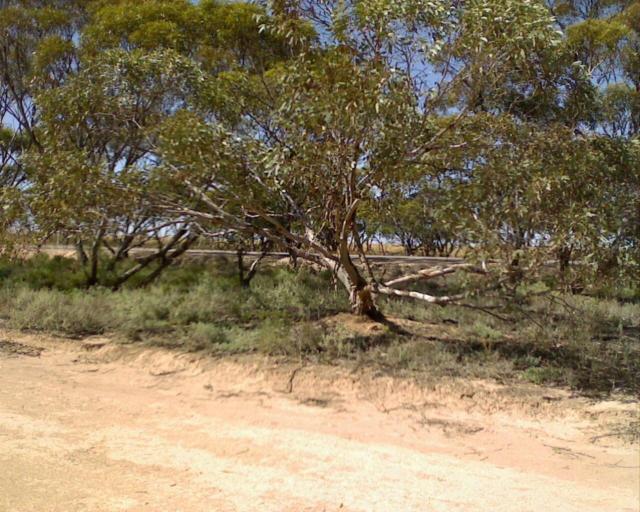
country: AU
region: South Australia
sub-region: Streaky Bay
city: Streaky Bay
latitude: -32.4720
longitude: 134.6188
